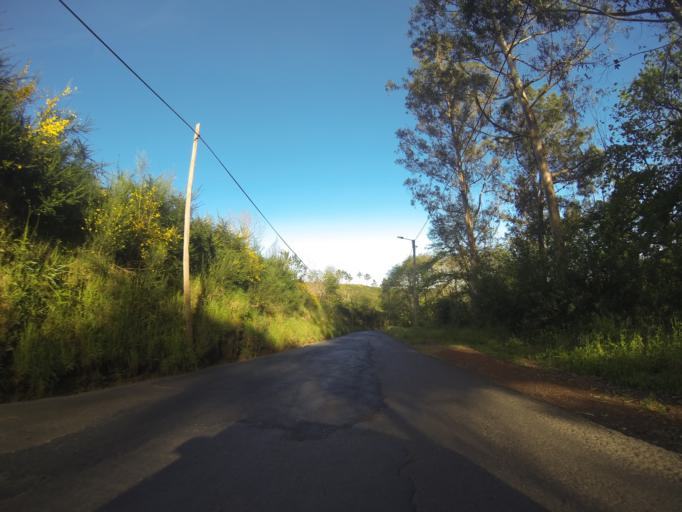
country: PT
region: Madeira
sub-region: Santa Cruz
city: Camacha
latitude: 32.6768
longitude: -16.8670
